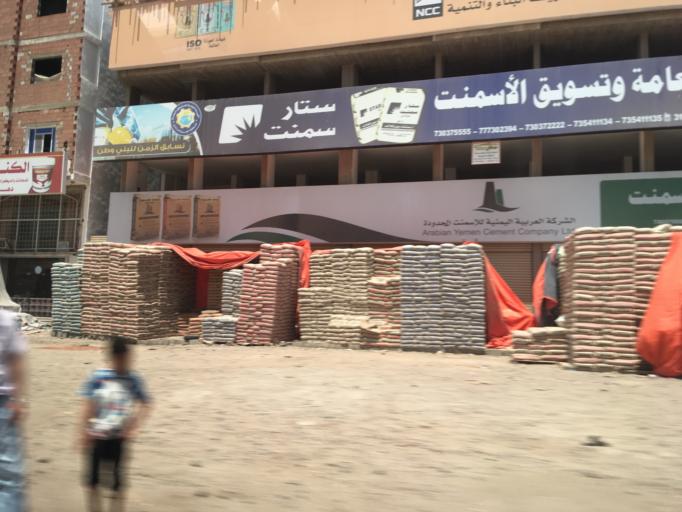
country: YE
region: Aden
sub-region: Al Mansura
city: Al Mansurah
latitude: 12.8704
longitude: 44.9719
